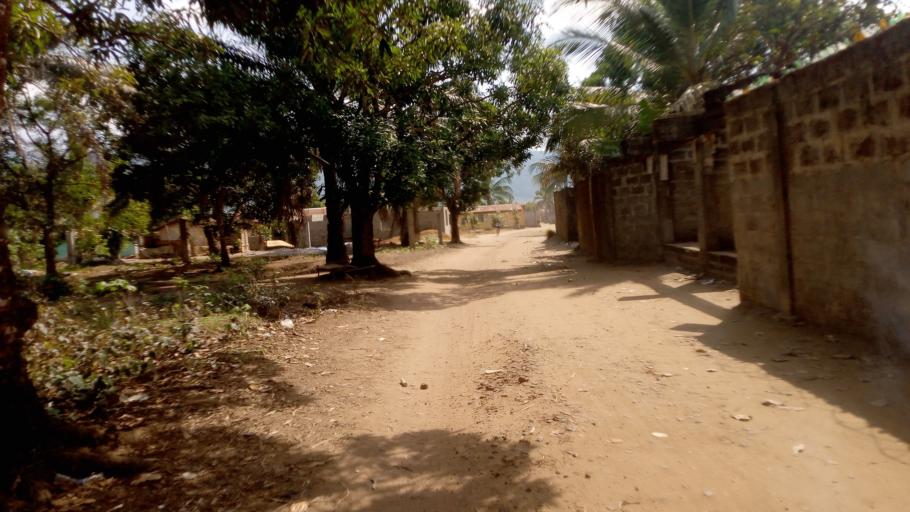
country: SL
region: Western Area
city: Waterloo
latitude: 8.3189
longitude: -13.0739
